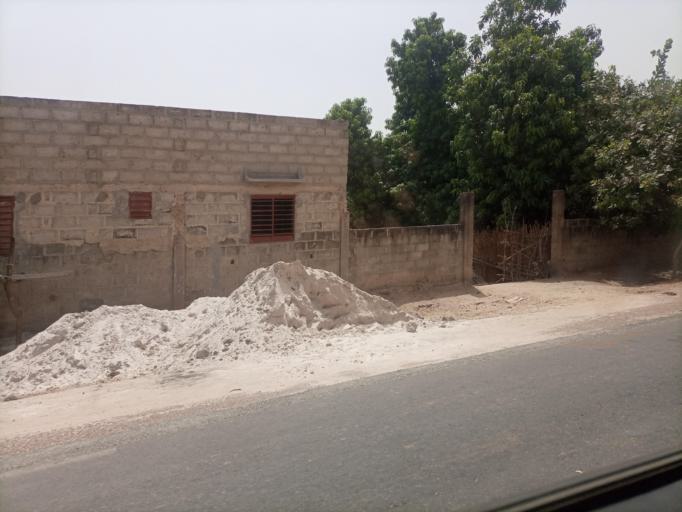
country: SN
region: Fatick
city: Sokone
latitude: 13.7105
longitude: -16.4277
